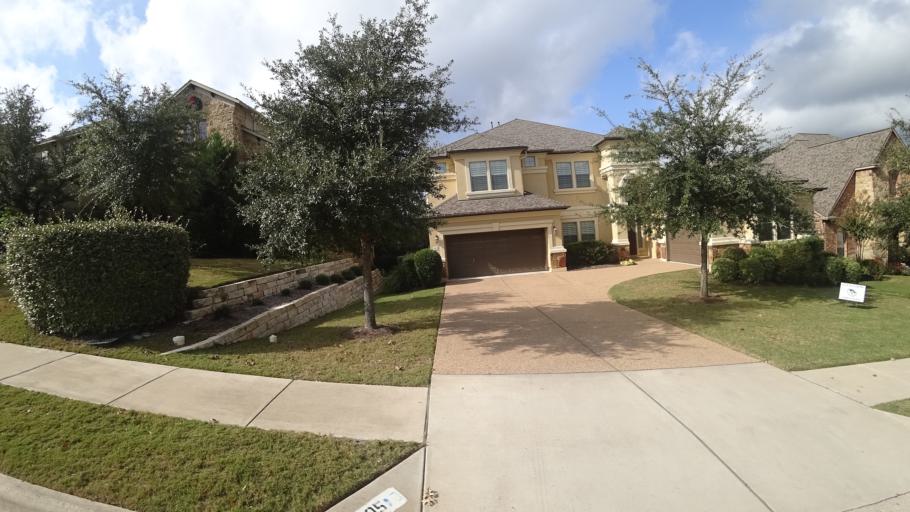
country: US
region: Texas
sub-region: Travis County
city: Barton Creek
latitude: 30.3151
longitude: -97.9004
